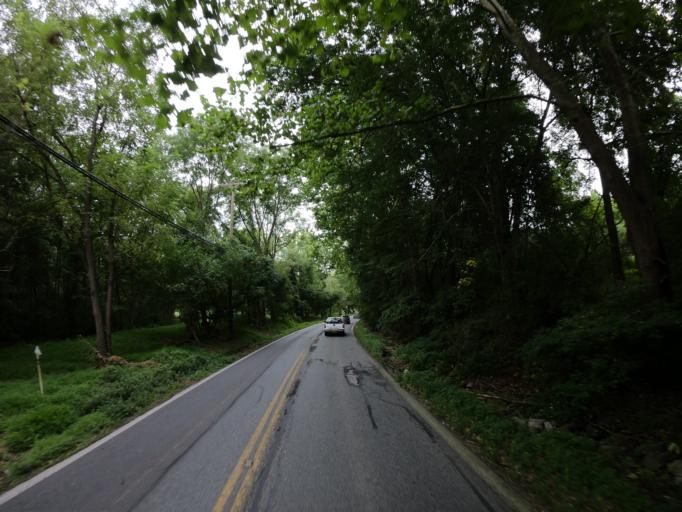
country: US
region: Maryland
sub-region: Montgomery County
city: Montgomery Village
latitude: 39.2036
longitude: -77.2061
